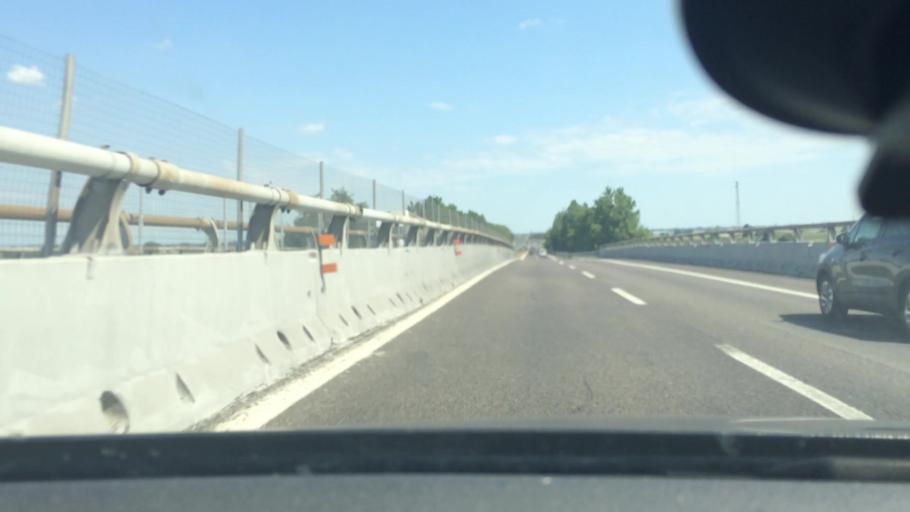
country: IT
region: Emilia-Romagna
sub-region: Provincia di Bologna
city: Malalbergo
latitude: 44.7349
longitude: 11.5177
